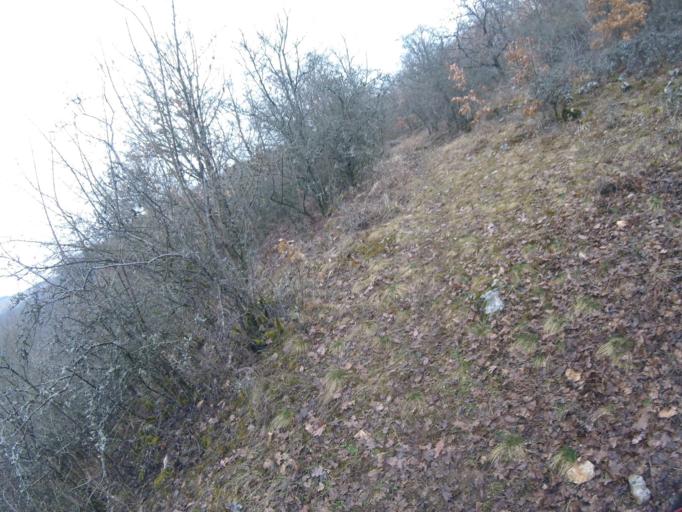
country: HU
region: Borsod-Abauj-Zemplen
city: Rudabanya
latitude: 48.4480
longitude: 20.6034
